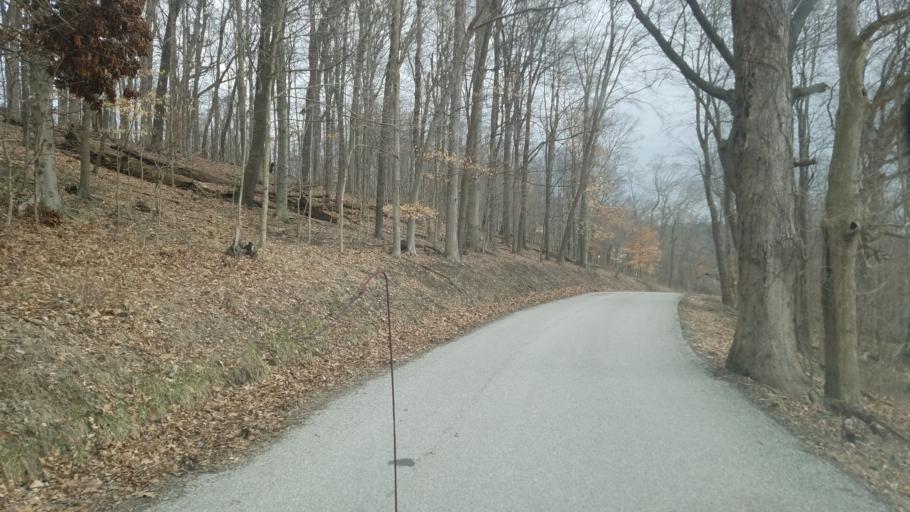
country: US
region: Ohio
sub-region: Licking County
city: Utica
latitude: 40.2038
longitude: -82.4190
